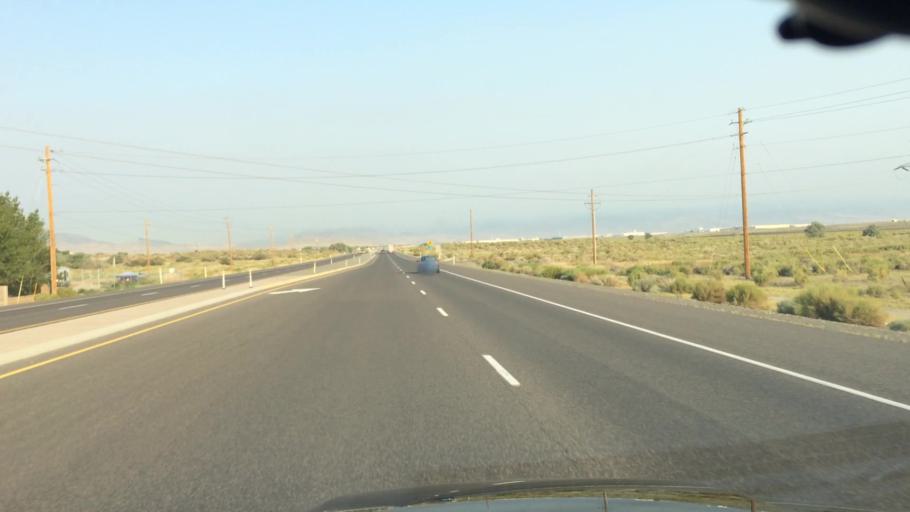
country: US
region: Nevada
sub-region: Lyon County
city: Fernley
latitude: 39.5935
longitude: -119.1601
